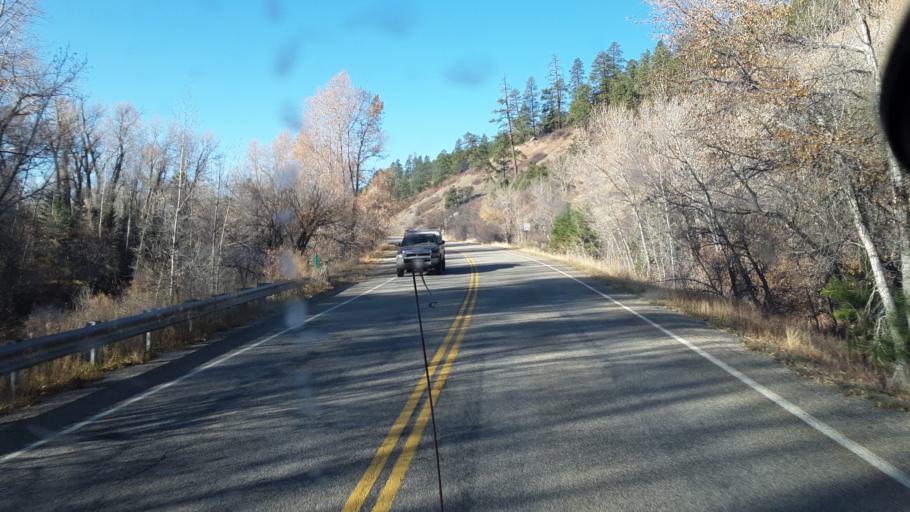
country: US
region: Colorado
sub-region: La Plata County
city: Durango
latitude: 37.3251
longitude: -107.7603
